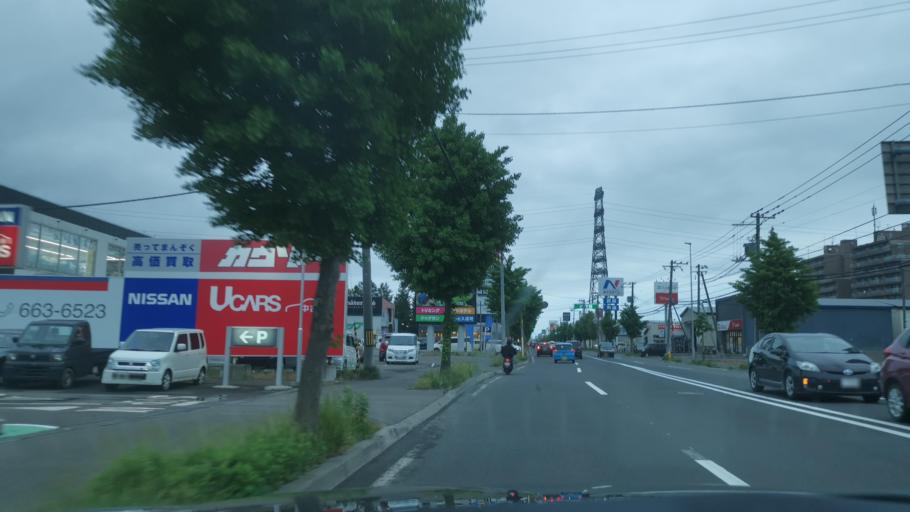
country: JP
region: Hokkaido
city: Sapporo
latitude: 43.1096
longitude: 141.2776
